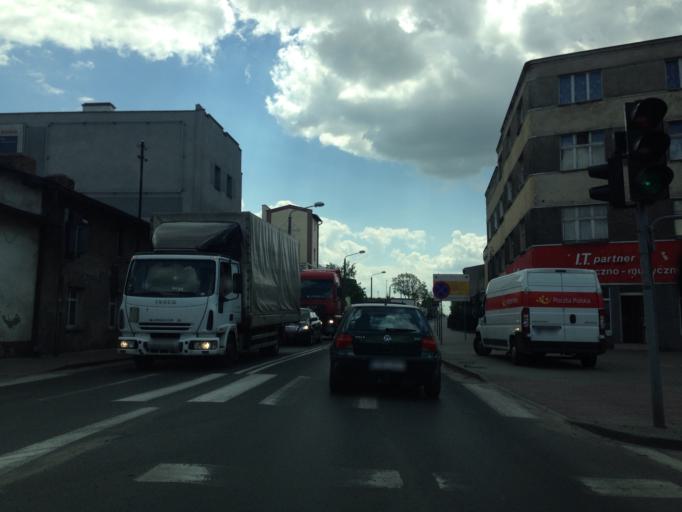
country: PL
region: Kujawsko-Pomorskie
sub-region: Powiat brodnicki
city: Brodnica
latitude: 53.2494
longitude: 19.3996
